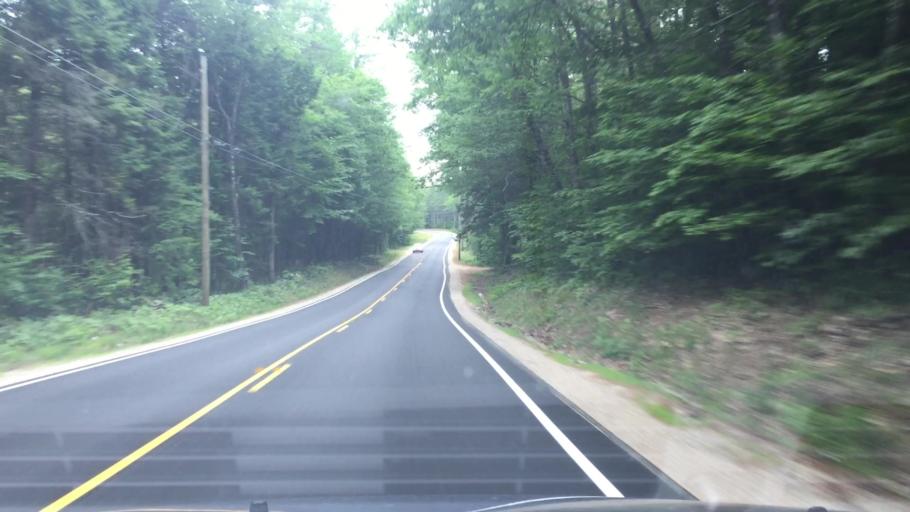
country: US
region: New Hampshire
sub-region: Carroll County
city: Freedom
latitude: 43.8327
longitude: -71.0773
